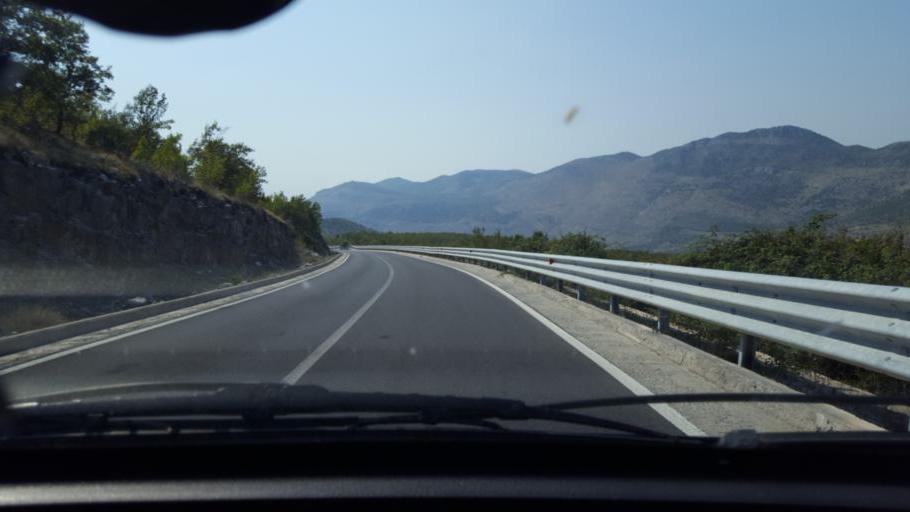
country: AL
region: Shkoder
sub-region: Rrethi i Malesia e Madhe
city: Kastrat
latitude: 42.3712
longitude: 19.4745
